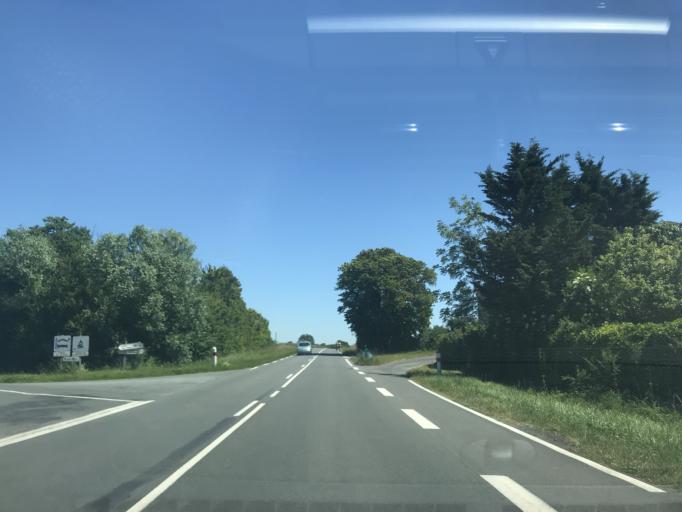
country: FR
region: Poitou-Charentes
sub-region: Departement de la Charente-Maritime
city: Meschers-sur-Gironde
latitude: 45.5545
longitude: -0.9206
